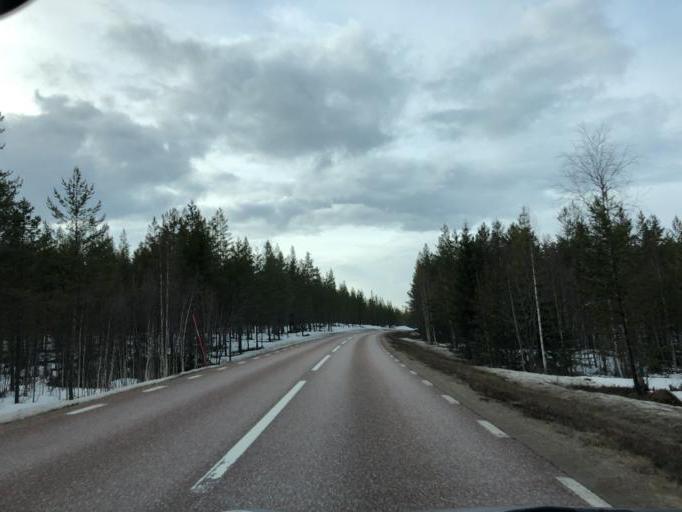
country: NO
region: Hedmark
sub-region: Trysil
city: Innbygda
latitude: 61.7093
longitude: 13.0121
